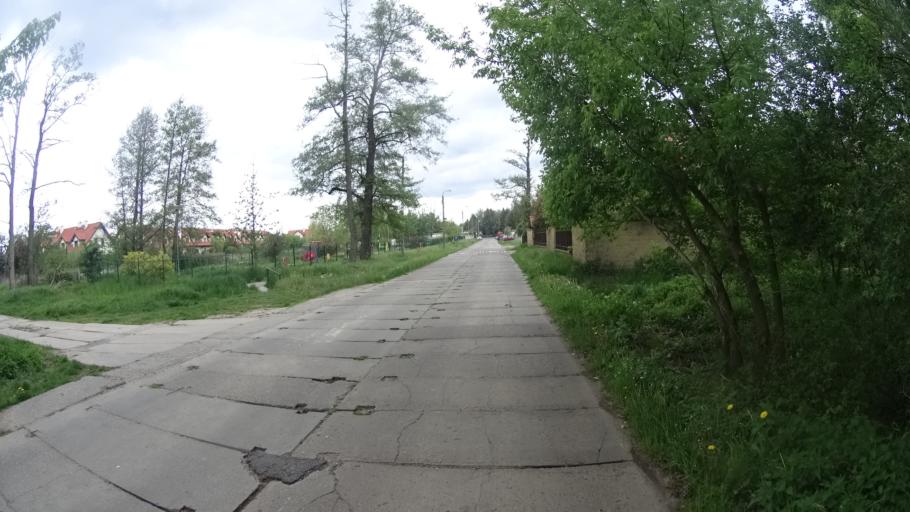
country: PL
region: Masovian Voivodeship
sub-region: Warszawa
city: Bemowo
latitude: 52.2837
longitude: 20.8868
